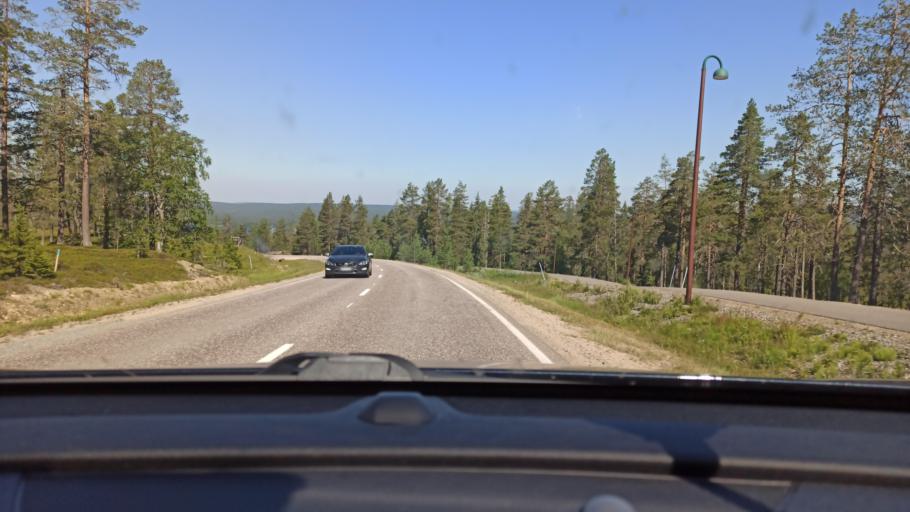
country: FI
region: Lapland
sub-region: Tunturi-Lappi
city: Kolari
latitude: 67.5918
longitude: 24.2007
